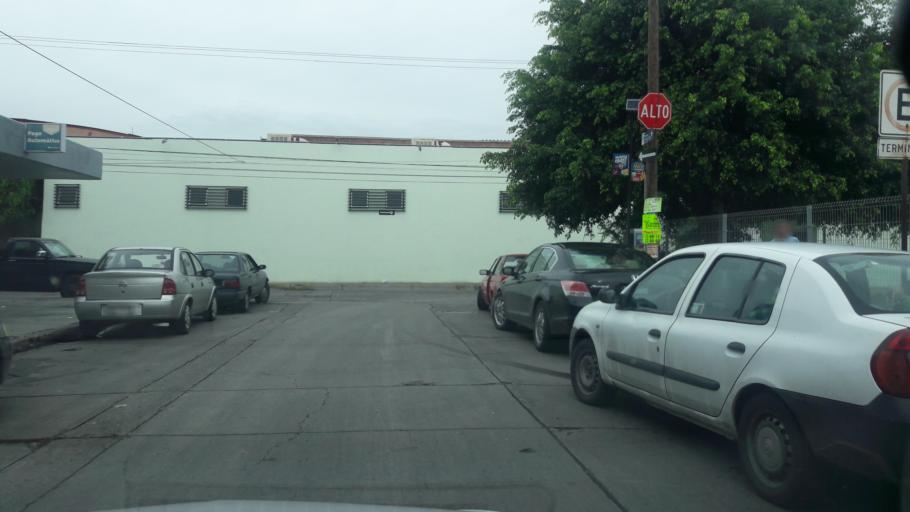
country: MX
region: Guanajuato
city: Leon
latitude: 21.1444
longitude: -101.6865
